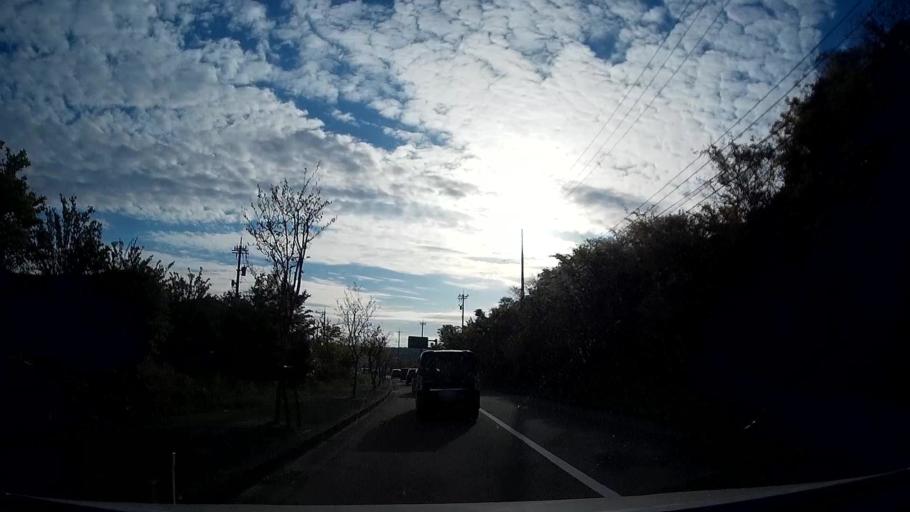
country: JP
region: Ishikawa
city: Nanao
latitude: 37.0840
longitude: 136.9294
